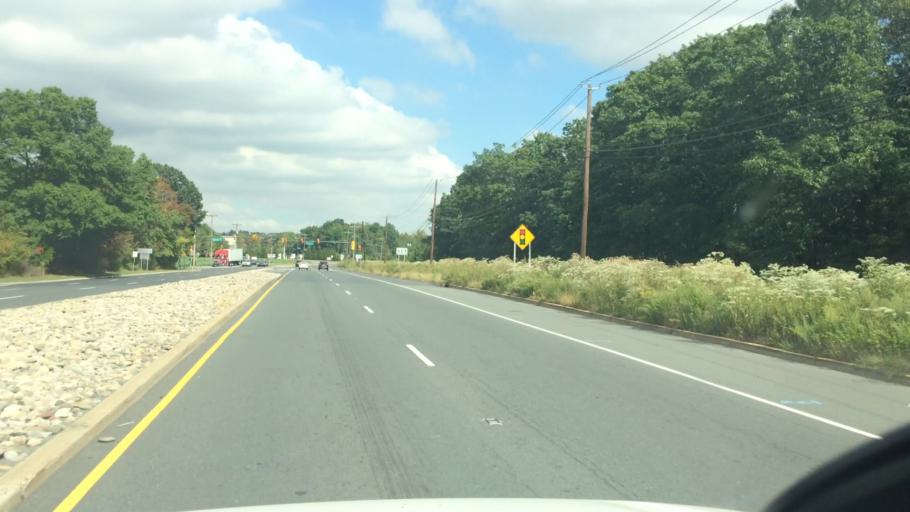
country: US
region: New Jersey
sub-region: Middlesex County
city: Fords
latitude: 40.5129
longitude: -74.3300
